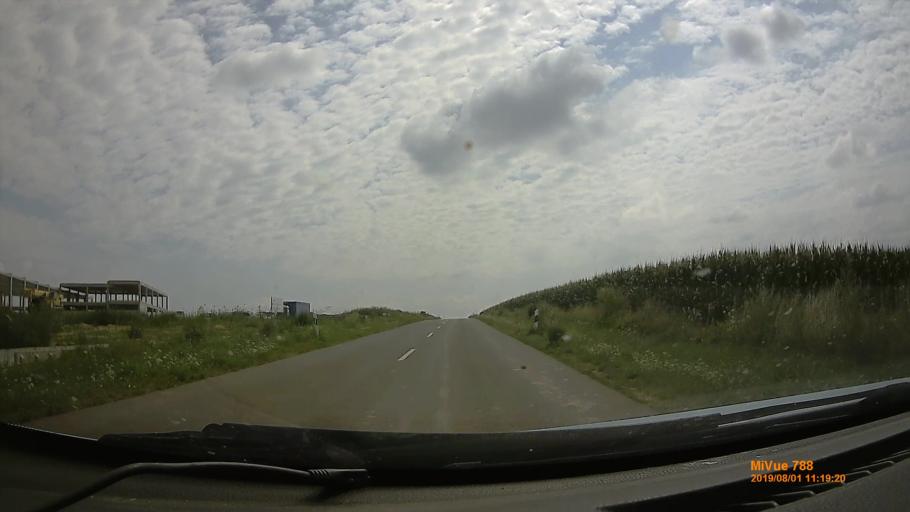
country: HU
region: Baranya
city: Kozarmisleny
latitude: 46.0091
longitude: 18.2263
